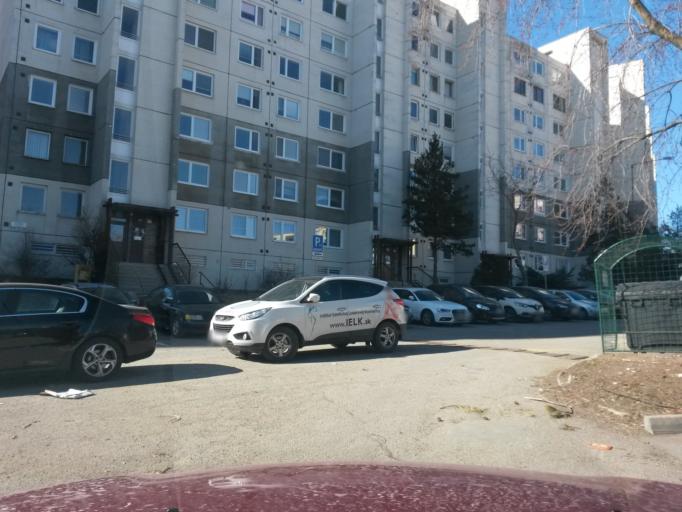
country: SK
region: Kosicky
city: Kosice
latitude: 48.7177
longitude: 21.2111
